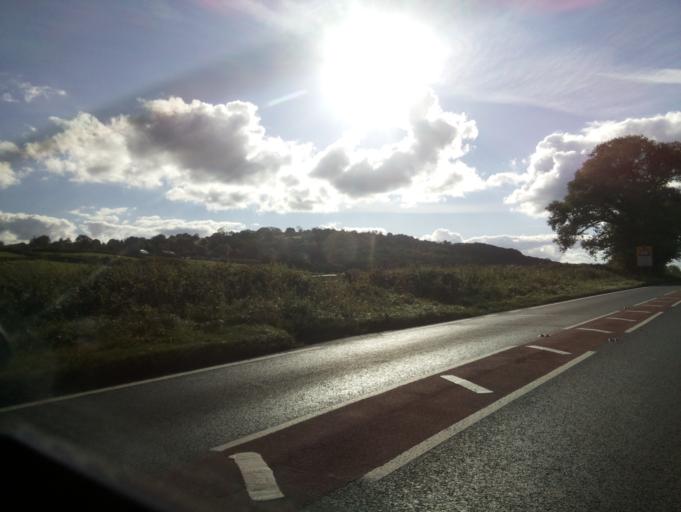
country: GB
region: Wales
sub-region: Sir Powys
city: Brecon
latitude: 51.9993
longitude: -3.2806
